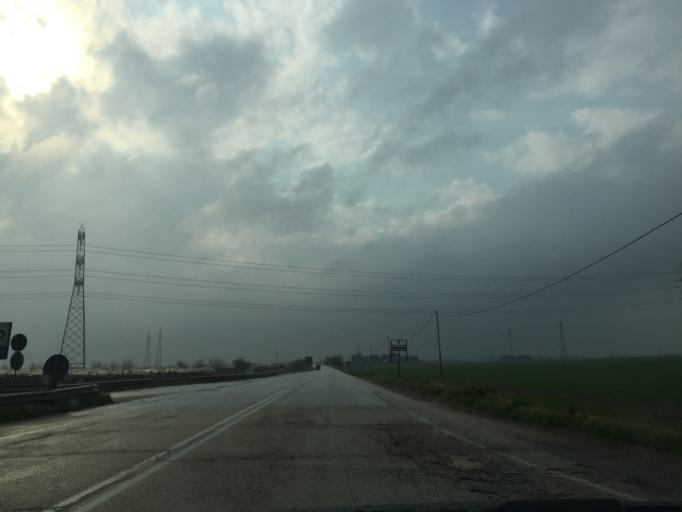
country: IT
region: Apulia
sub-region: Provincia di Foggia
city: Foggia
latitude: 41.4972
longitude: 15.5196
